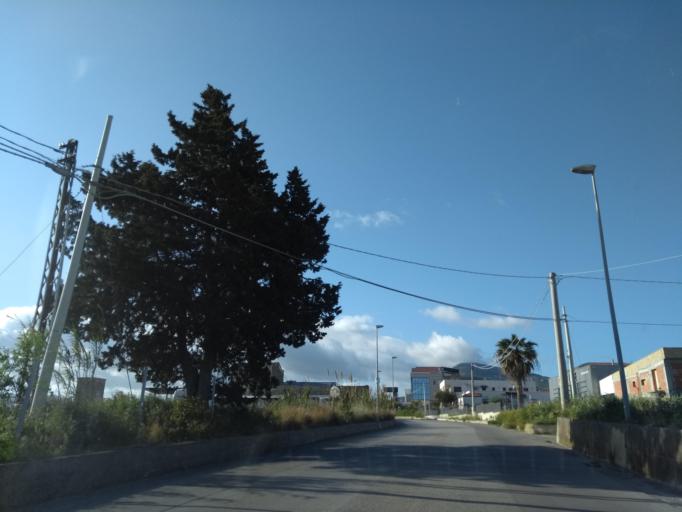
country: IT
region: Sicily
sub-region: Trapani
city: Alcamo
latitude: 38.0027
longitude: 12.9555
